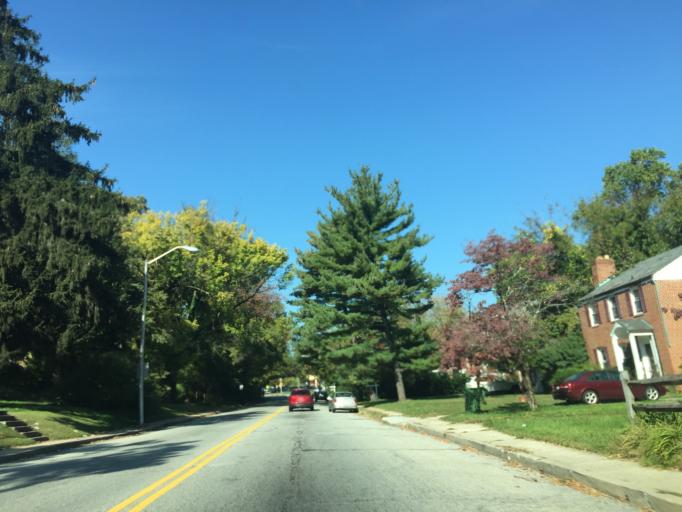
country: US
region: Maryland
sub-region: Baltimore County
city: Towson
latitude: 39.3633
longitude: -76.6057
